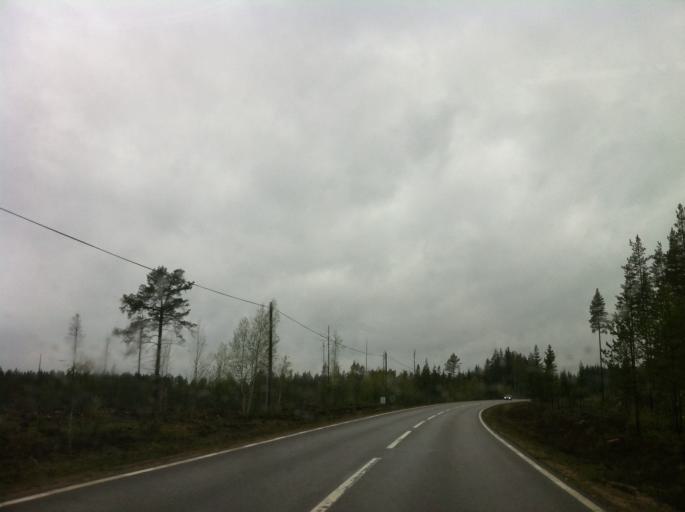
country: SE
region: Jaemtland
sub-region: Harjedalens Kommun
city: Sveg
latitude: 62.1464
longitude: 13.9256
